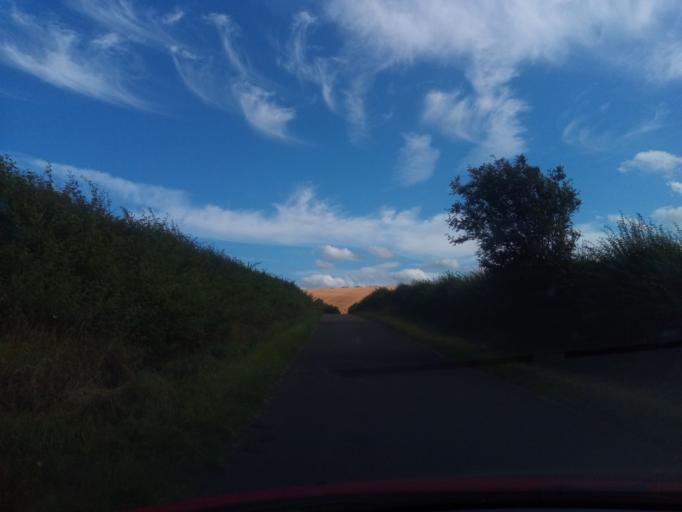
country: GB
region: Scotland
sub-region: The Scottish Borders
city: Coldstream
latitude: 55.6209
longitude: -2.1936
